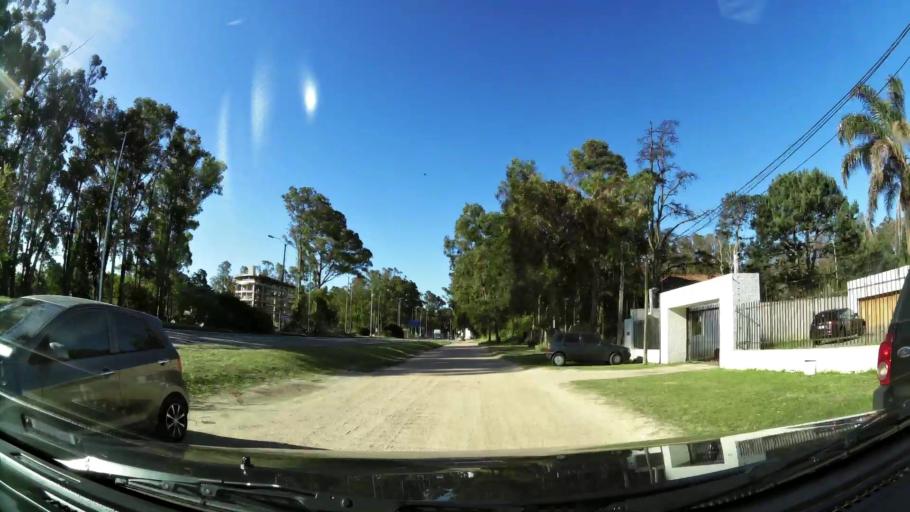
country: UY
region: Canelones
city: Barra de Carrasco
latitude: -34.8613
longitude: -56.0300
